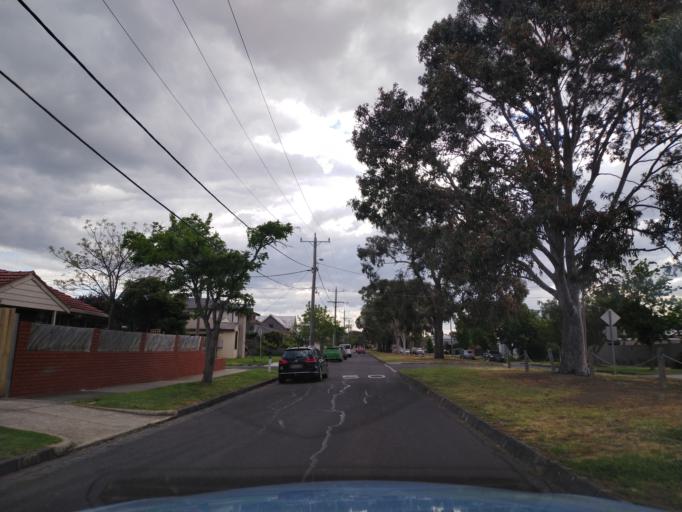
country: AU
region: Victoria
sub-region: Hobsons Bay
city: Williamstown North
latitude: -37.8476
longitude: 144.8719
